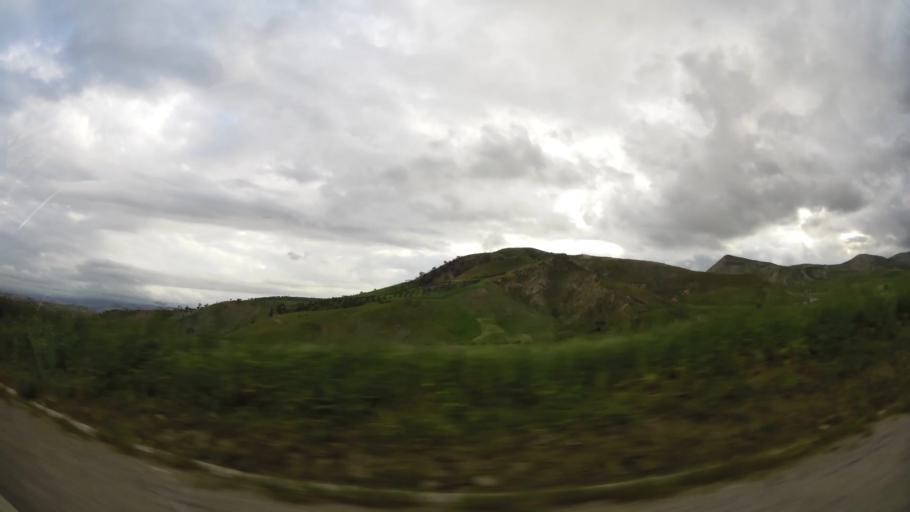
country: MA
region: Taza-Al Hoceima-Taounate
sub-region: Taza
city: Taza
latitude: 34.2871
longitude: -3.9627
